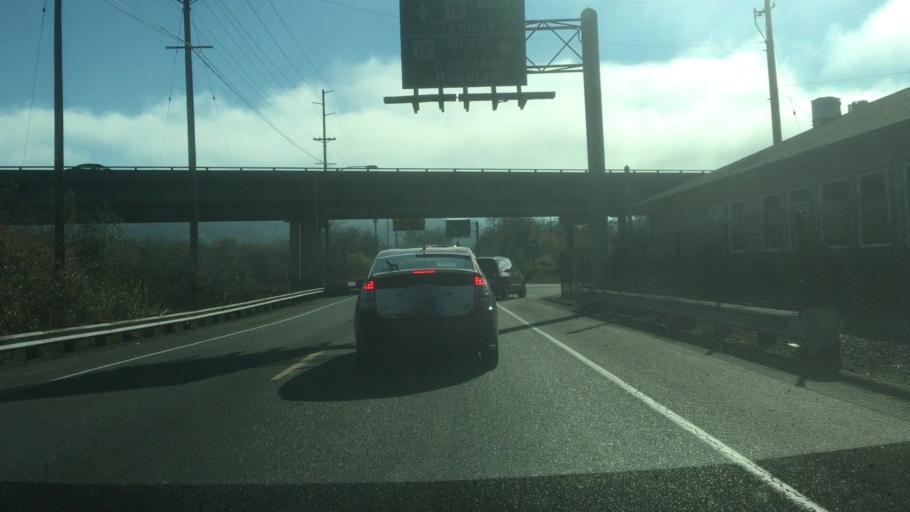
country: US
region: Washington
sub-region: Grays Harbor County
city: Montesano
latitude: 46.9764
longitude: -123.6010
